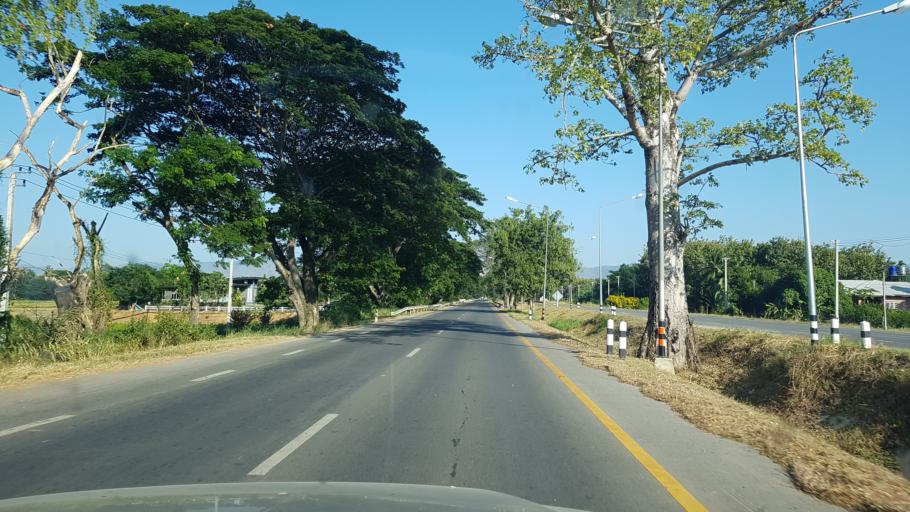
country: TH
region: Phetchabun
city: Lom Sak
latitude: 16.7267
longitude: 101.2482
